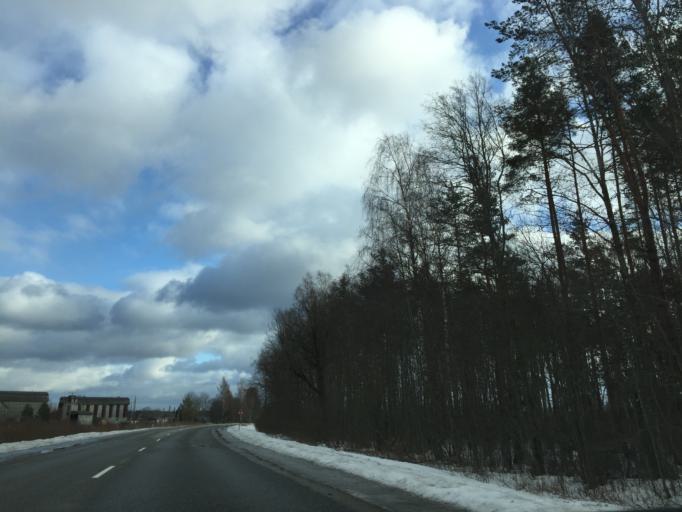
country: LV
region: Aloja
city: Staicele
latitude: 57.8455
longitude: 24.7274
